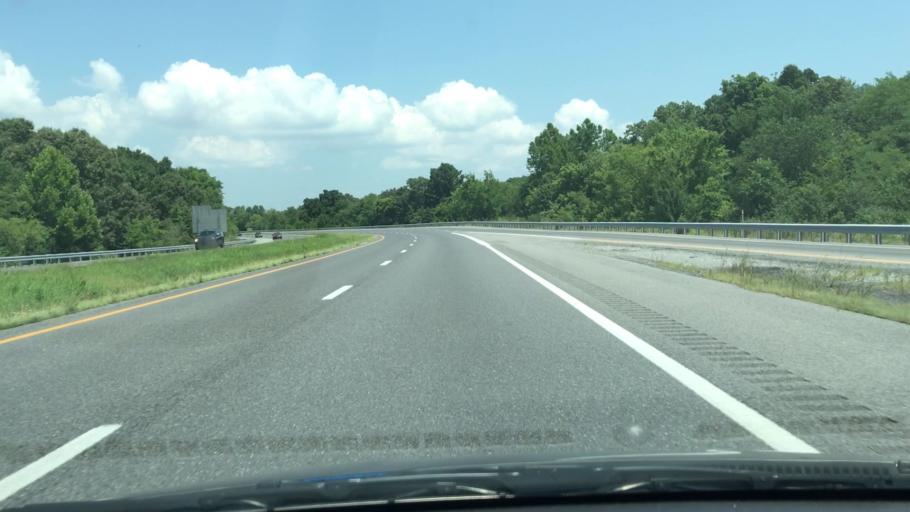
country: US
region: Kentucky
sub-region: Marshall County
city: Benton
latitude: 36.9306
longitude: -88.3442
